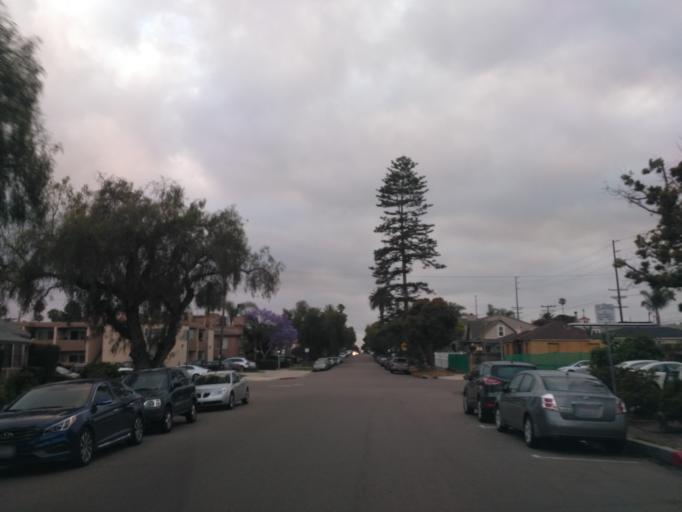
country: US
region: California
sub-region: San Diego County
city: La Jolla
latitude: 32.7998
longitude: -117.2364
